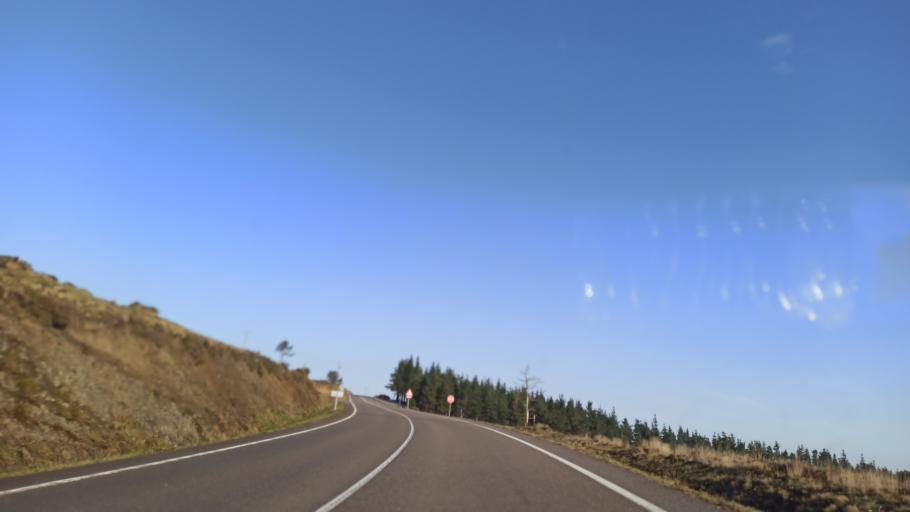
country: ES
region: Galicia
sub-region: Provincia da Coruna
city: As Pontes de Garcia Rodriguez
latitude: 43.5120
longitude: -7.8176
